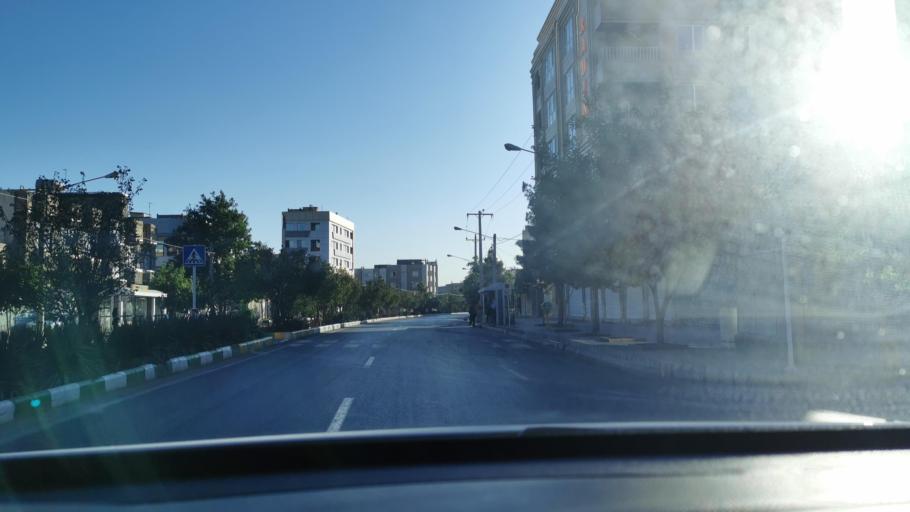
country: IR
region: Razavi Khorasan
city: Mashhad
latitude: 36.3492
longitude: 59.4783
